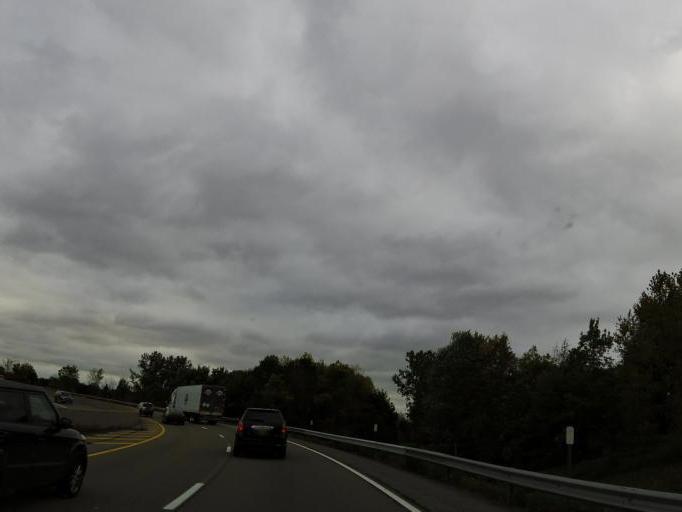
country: US
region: New York
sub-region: Erie County
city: West Seneca
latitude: 42.8509
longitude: -78.7929
